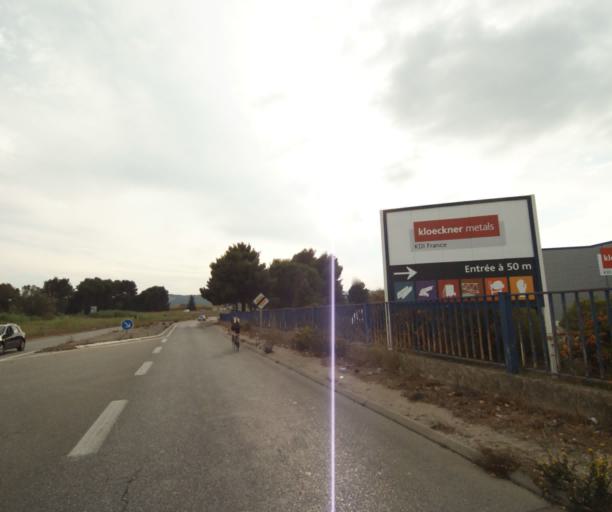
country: FR
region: Provence-Alpes-Cote d'Azur
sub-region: Departement des Bouches-du-Rhone
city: Marignane
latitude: 43.3952
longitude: 5.1961
